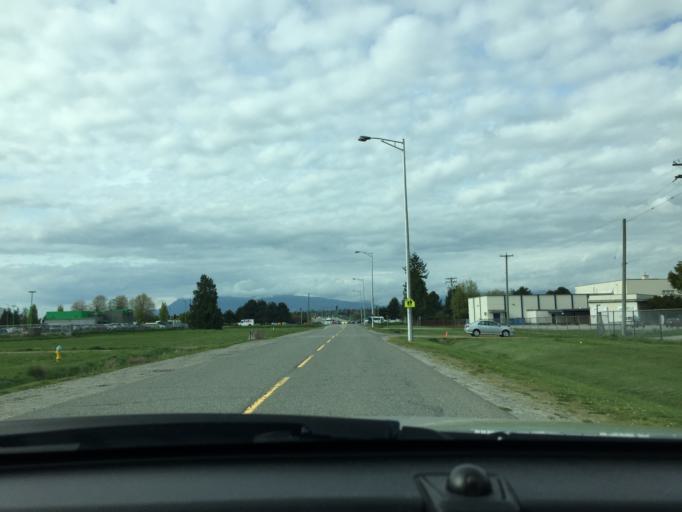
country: CA
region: British Columbia
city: Richmond
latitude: 49.1898
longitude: -123.1508
